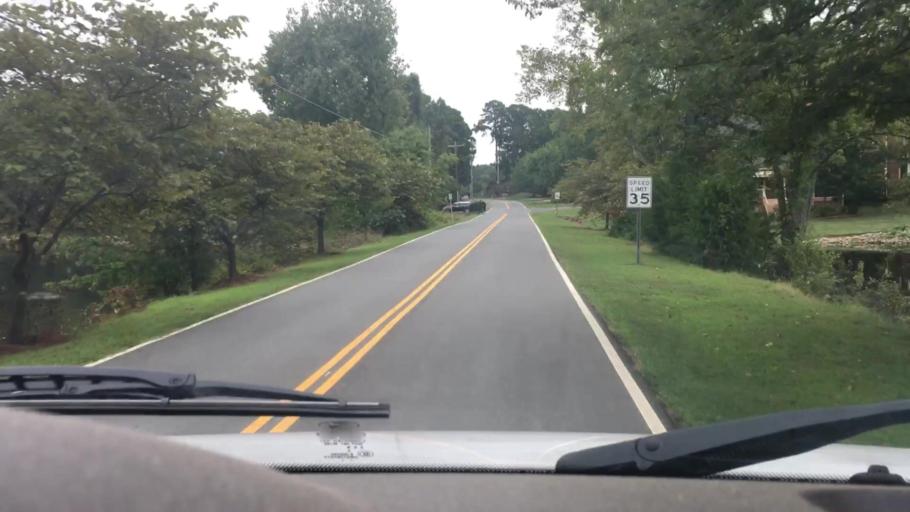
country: US
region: North Carolina
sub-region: Mecklenburg County
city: Cornelius
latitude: 35.4463
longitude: -80.9027
